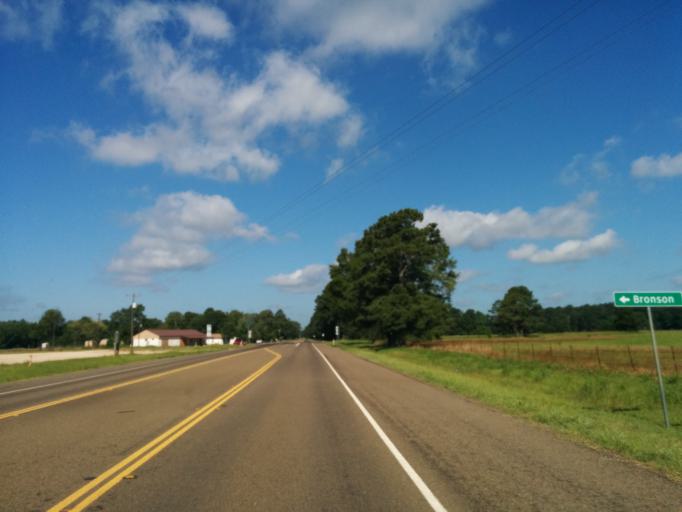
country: US
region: Texas
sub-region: Sabine County
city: Milam
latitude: 31.4127
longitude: -93.9961
